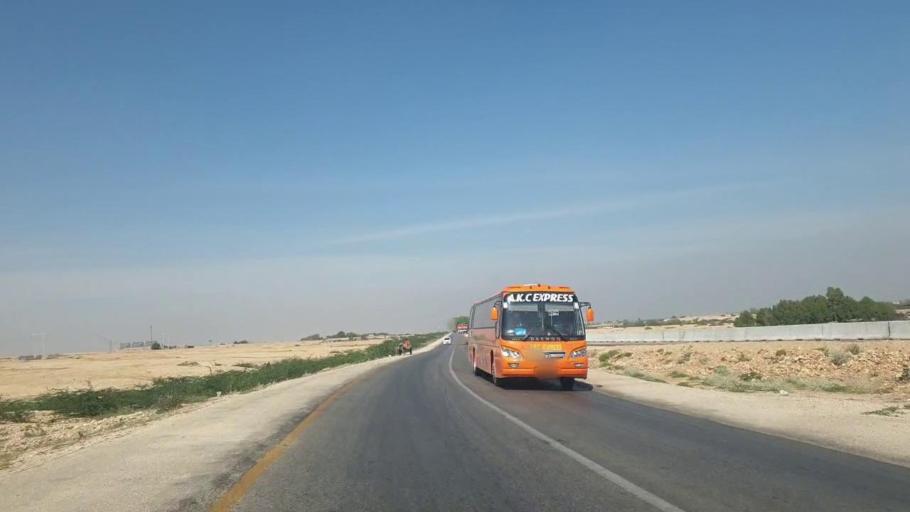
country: PK
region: Sindh
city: Matiari
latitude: 25.6852
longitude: 68.2953
